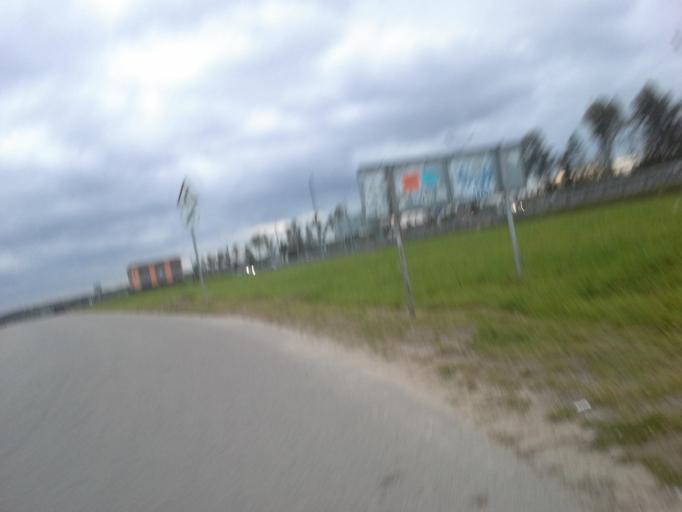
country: RU
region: Moskovskaya
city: Kokoshkino
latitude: 55.6222
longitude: 37.1463
